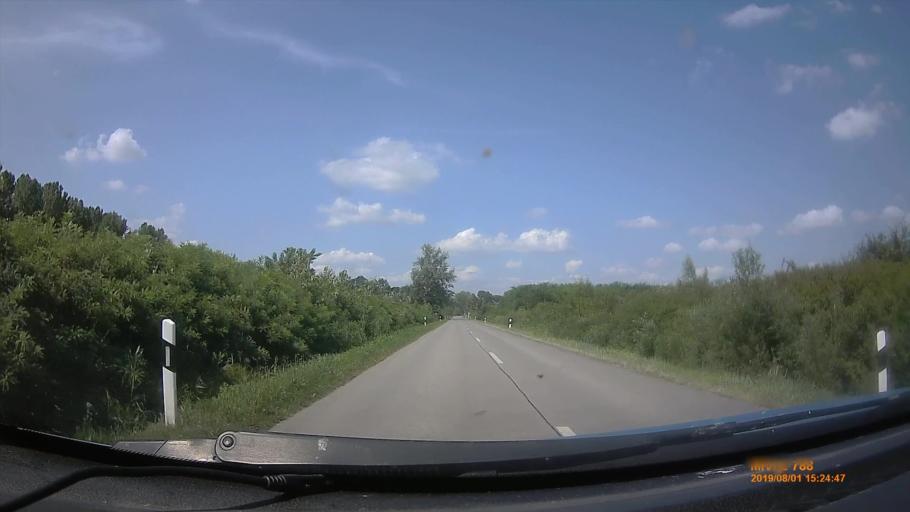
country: HU
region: Baranya
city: Sellye
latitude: 45.8877
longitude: 17.8525
